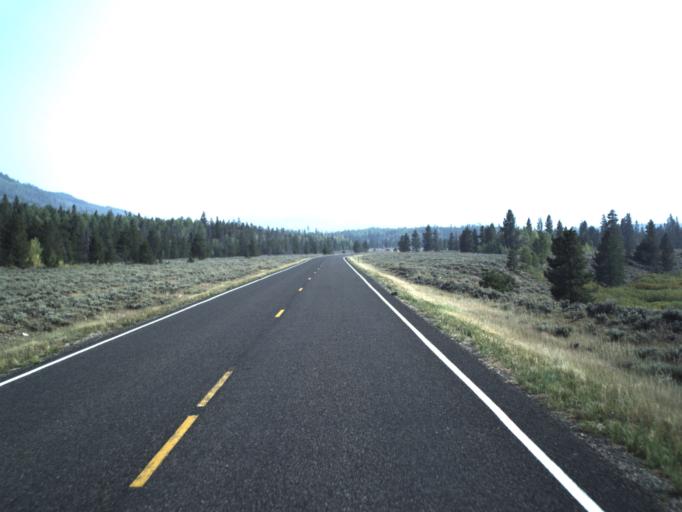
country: US
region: Wyoming
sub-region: Uinta County
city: Evanston
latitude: 40.8806
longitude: -110.8315
